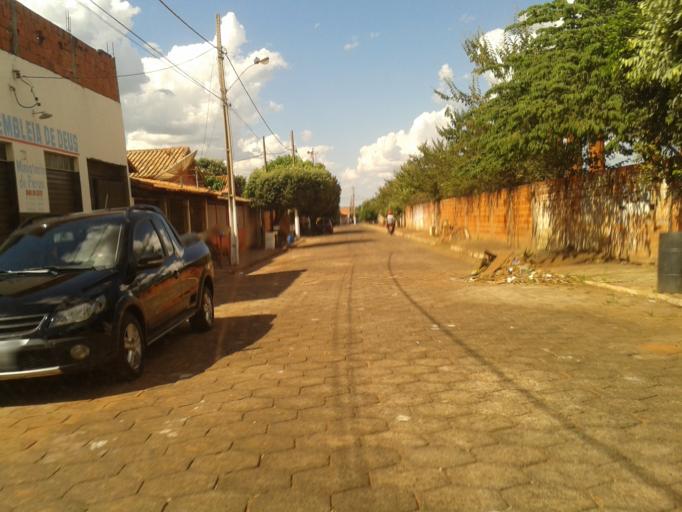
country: BR
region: Minas Gerais
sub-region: Santa Vitoria
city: Santa Vitoria
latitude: -18.6907
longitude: -49.9472
